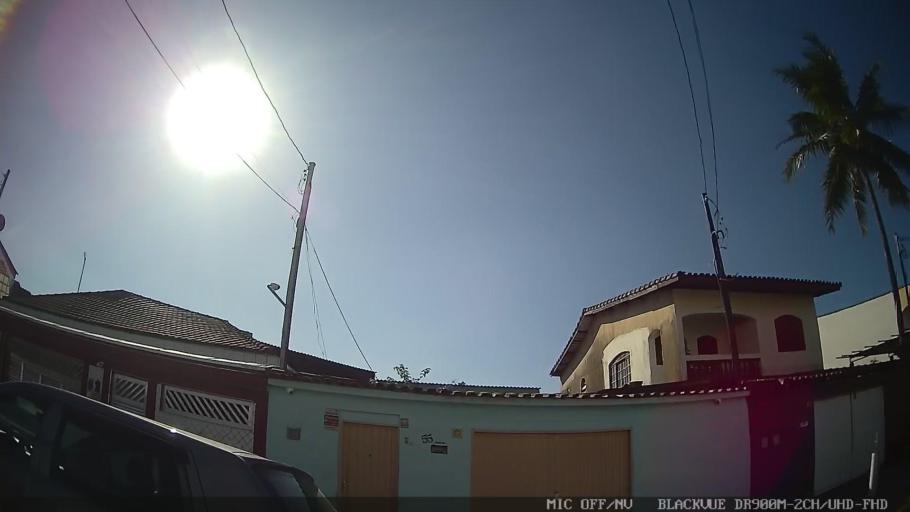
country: BR
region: Sao Paulo
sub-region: Santos
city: Santos
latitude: -23.9522
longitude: -46.2961
